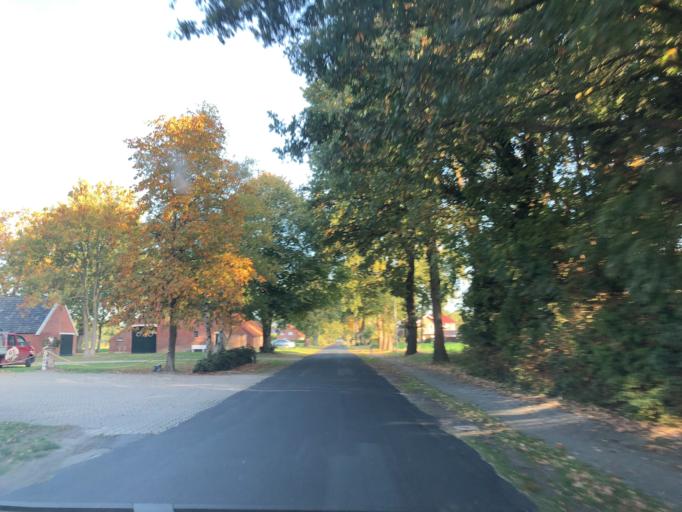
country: DE
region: Lower Saxony
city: Lehe
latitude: 53.0377
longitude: 7.3462
